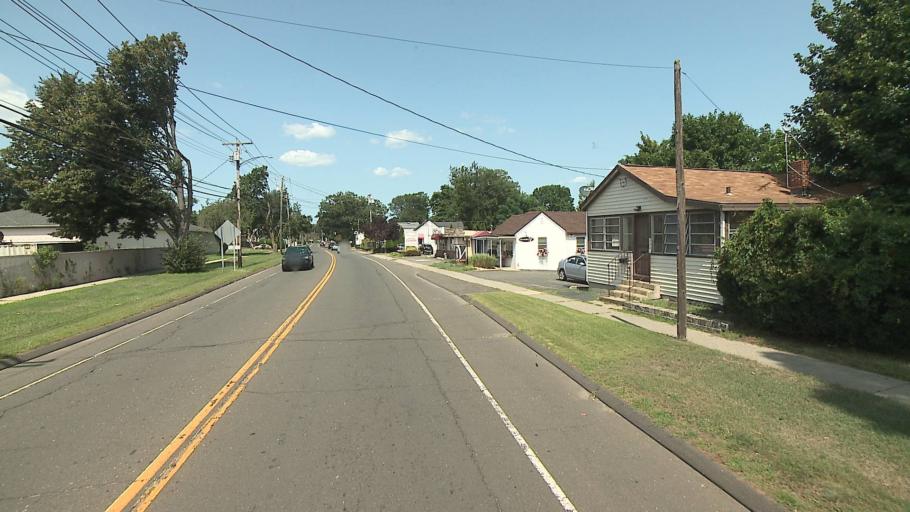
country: US
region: Connecticut
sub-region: Fairfield County
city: Stratford
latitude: 41.2042
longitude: -73.1182
